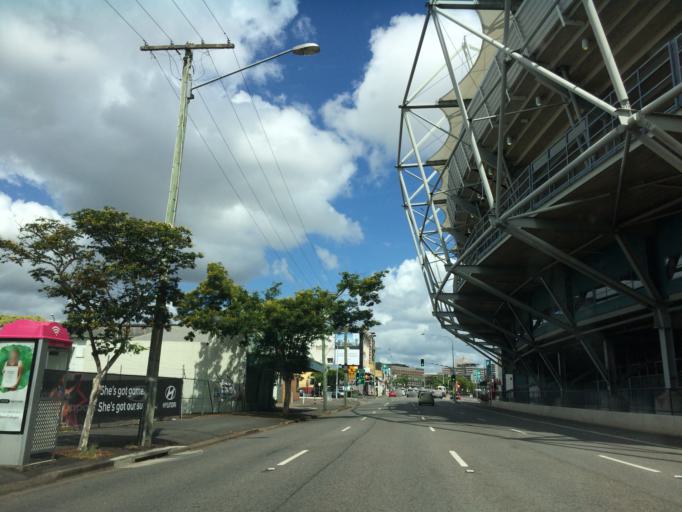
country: AU
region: Queensland
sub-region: Brisbane
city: Woolloongabba
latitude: -27.4869
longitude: 153.0384
